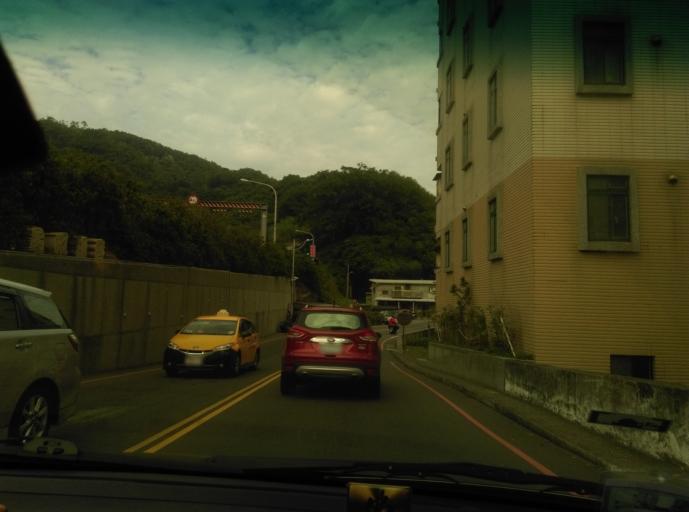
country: TW
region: Taiwan
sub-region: Keelung
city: Keelung
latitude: 25.1916
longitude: 121.6839
